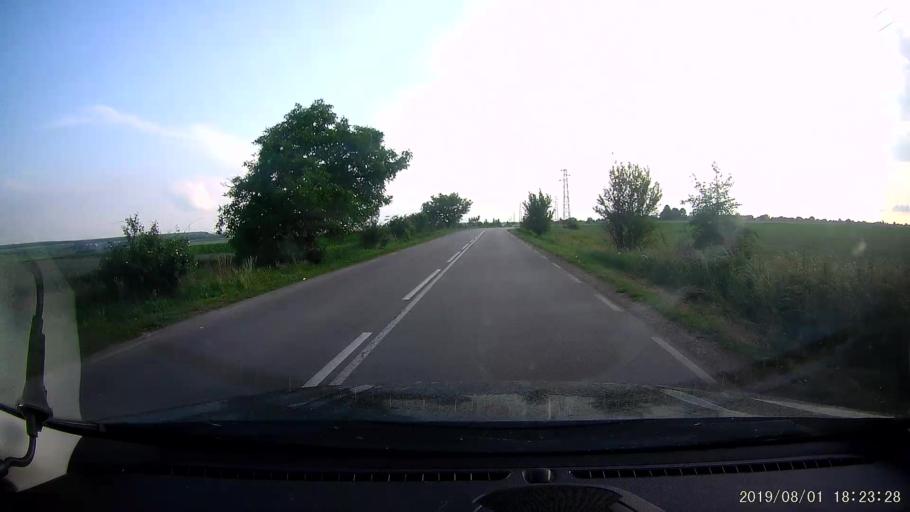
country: BG
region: Shumen
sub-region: Obshtina Kaolinovo
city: Kaolinovo
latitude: 43.6284
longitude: 27.0242
